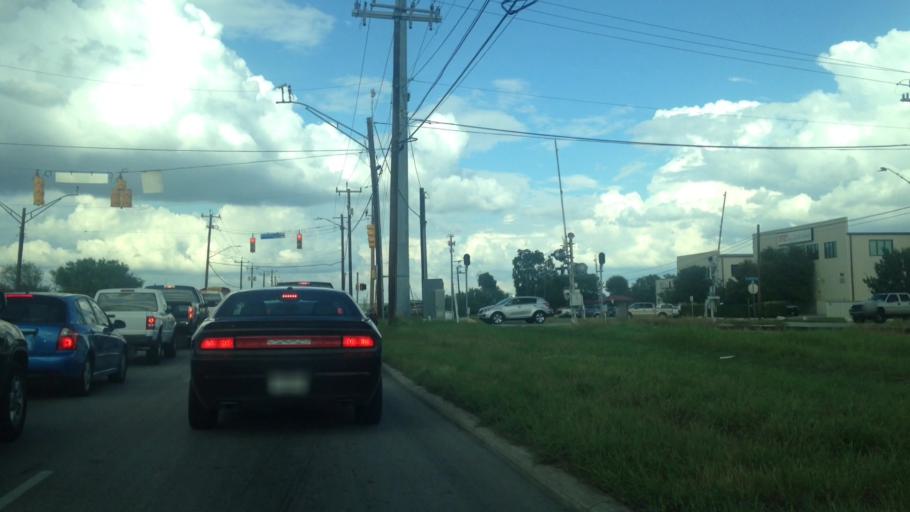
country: US
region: Texas
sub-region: Bexar County
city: Alamo Heights
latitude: 29.5352
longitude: -98.4524
